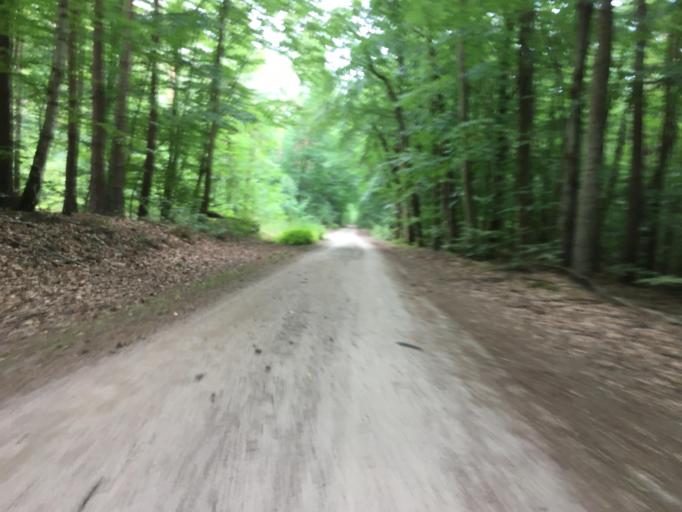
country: DE
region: Brandenburg
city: Lychen
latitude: 53.1094
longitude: 13.2762
